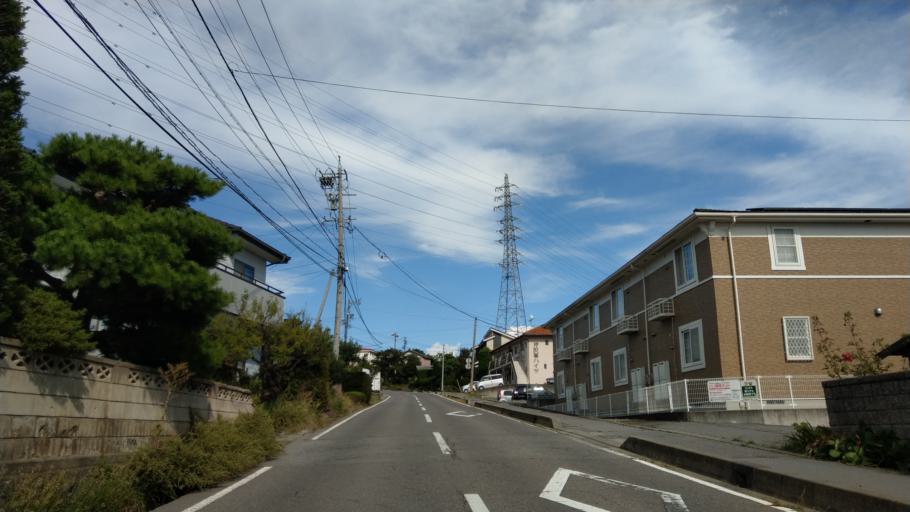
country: JP
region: Nagano
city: Komoro
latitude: 36.3285
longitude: 138.4387
